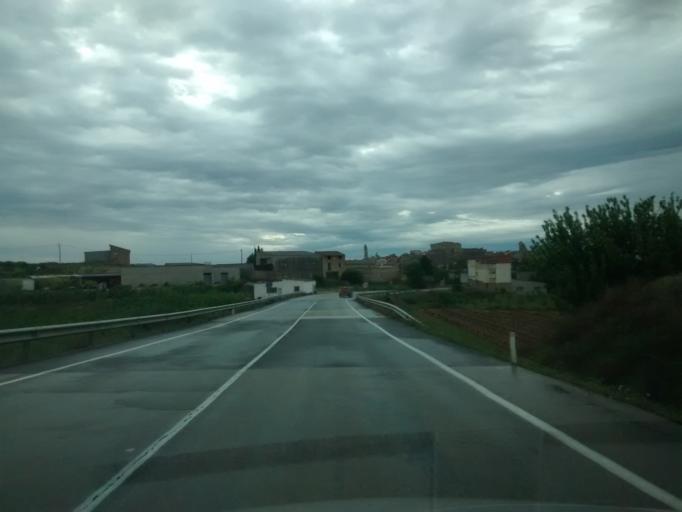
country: ES
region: Aragon
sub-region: Provincia de Zaragoza
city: Maella
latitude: 41.1156
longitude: 0.1473
